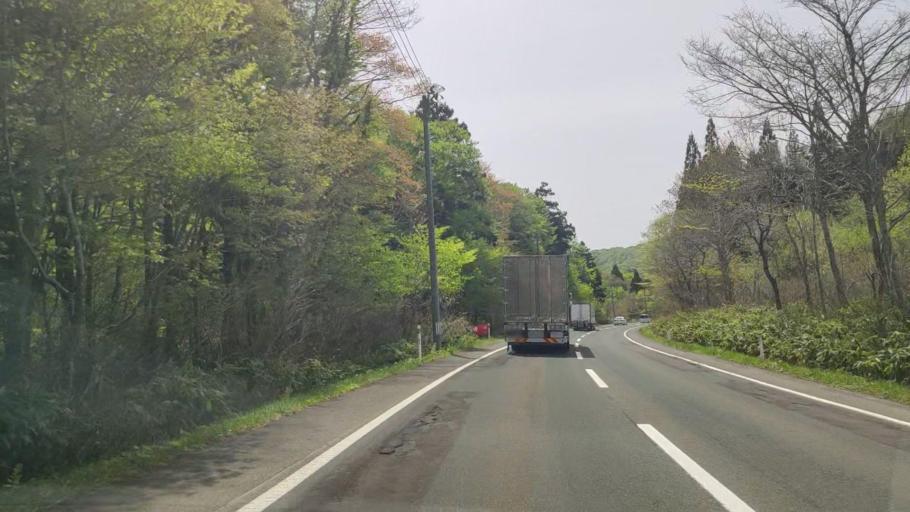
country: JP
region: Aomori
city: Aomori Shi
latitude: 40.7795
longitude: 141.0301
